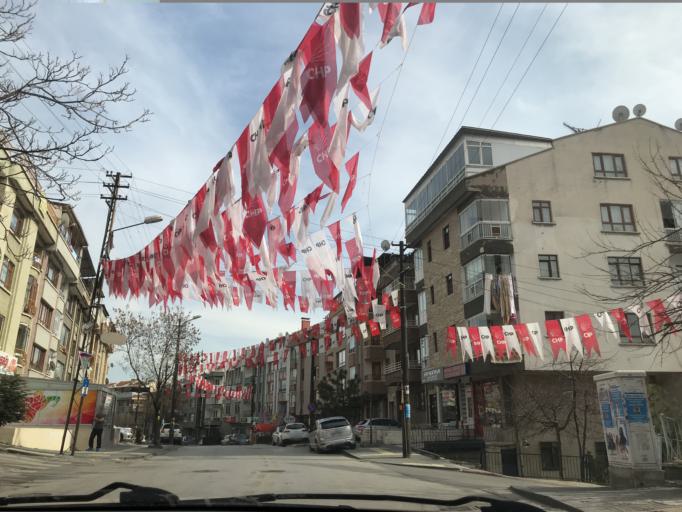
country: TR
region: Ankara
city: Batikent
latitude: 39.9660
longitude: 32.8003
